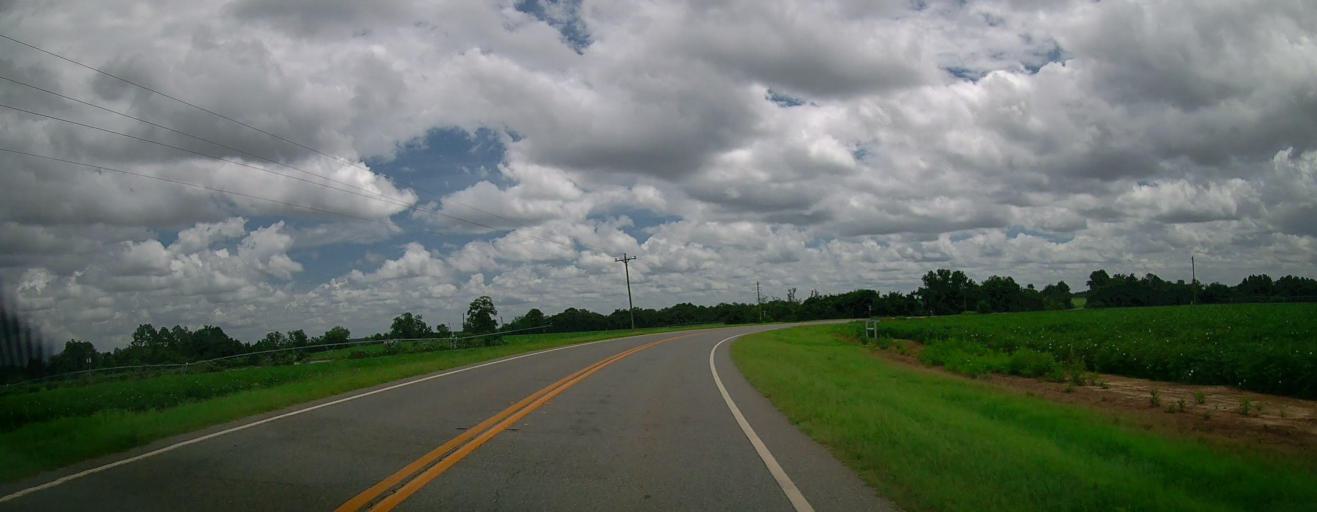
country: US
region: Georgia
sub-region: Wilcox County
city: Rochelle
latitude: 32.0210
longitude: -83.5583
